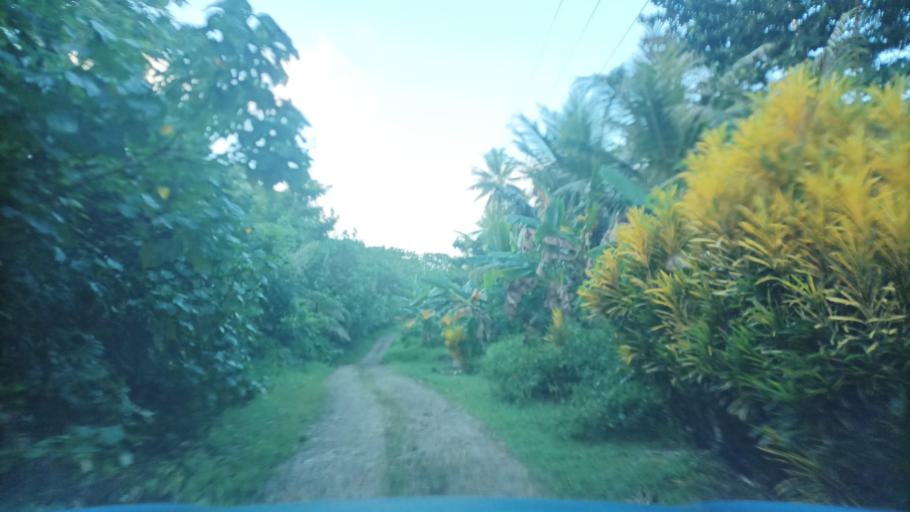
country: FM
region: Pohnpei
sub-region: Kolonia Municipality
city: Kolonia Town
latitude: 6.9775
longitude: 158.1811
